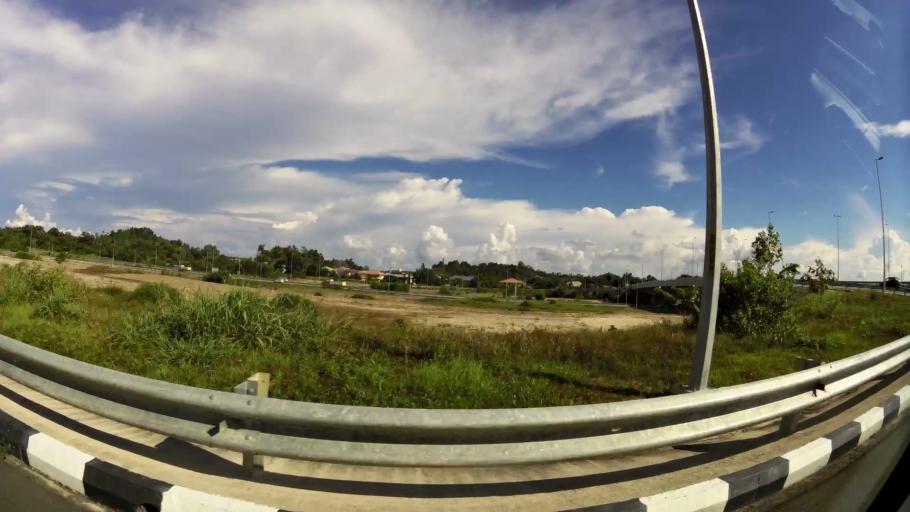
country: BN
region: Brunei and Muara
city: Bandar Seri Begawan
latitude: 4.9880
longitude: 114.9604
